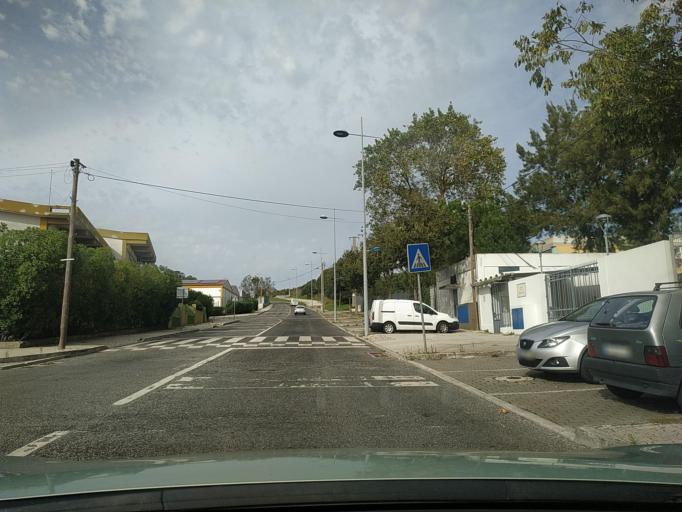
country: PT
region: Lisbon
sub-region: Amadora
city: Amadora
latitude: 38.7685
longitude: -9.2394
